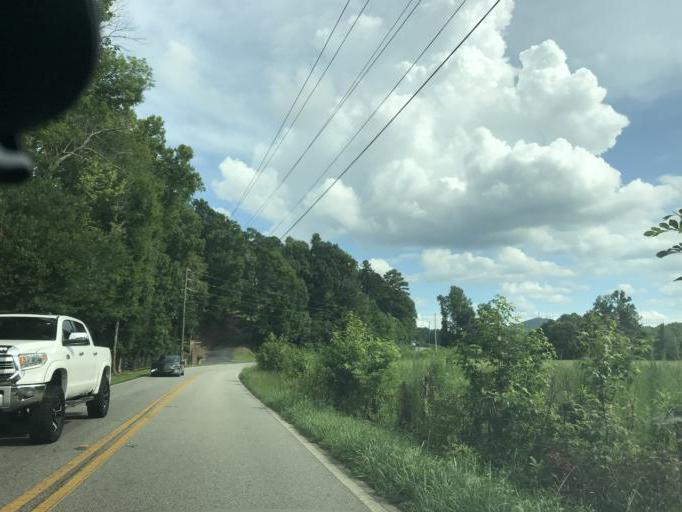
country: US
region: Georgia
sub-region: Forsyth County
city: Cumming
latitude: 34.2757
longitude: -84.1524
